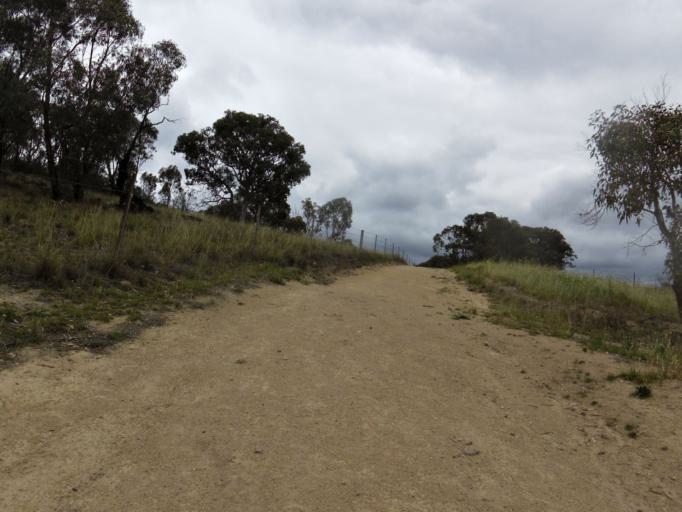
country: AU
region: Australian Capital Territory
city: Macquarie
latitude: -35.3505
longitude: 149.0218
